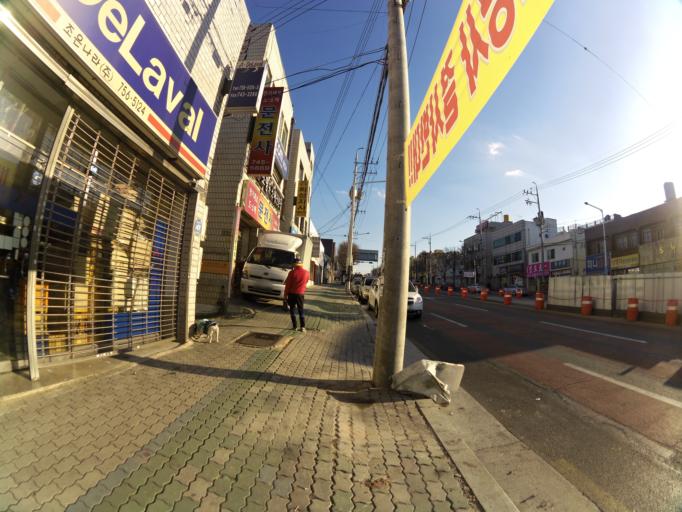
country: KR
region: Daegu
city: Daegu
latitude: 35.8773
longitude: 128.6325
